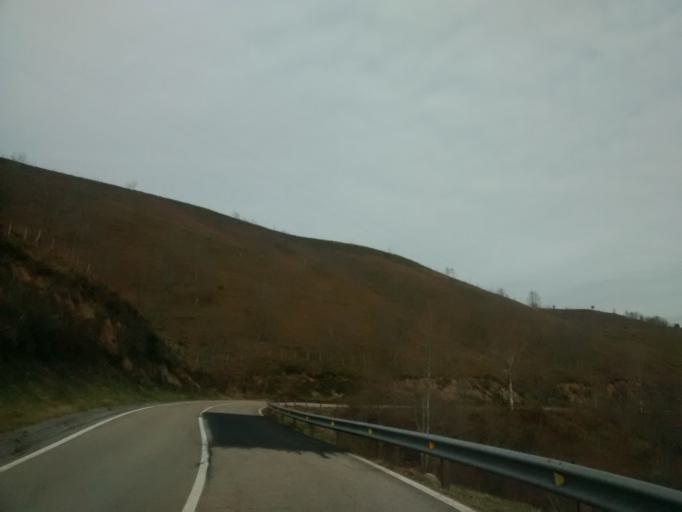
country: ES
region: Cantabria
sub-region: Provincia de Cantabria
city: Ruente
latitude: 43.2481
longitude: -4.3391
